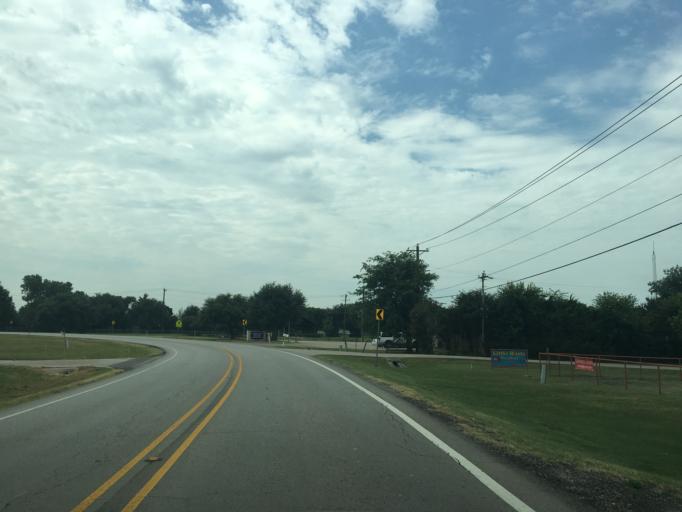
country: US
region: Texas
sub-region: Collin County
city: Lucas
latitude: 33.0943
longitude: -96.5938
